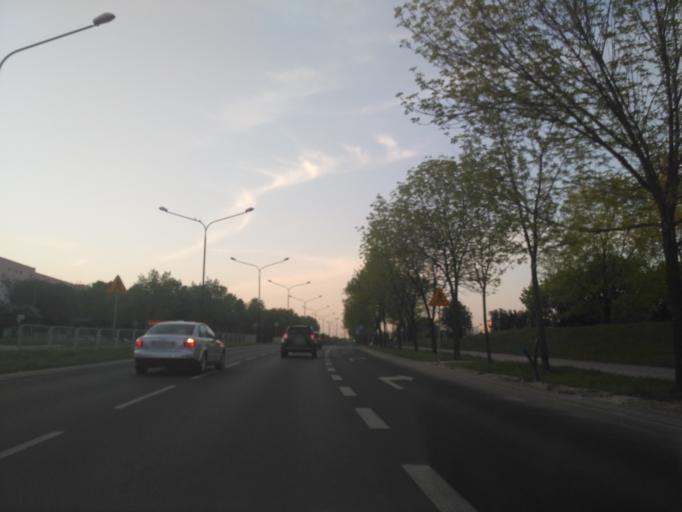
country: PL
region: Lublin Voivodeship
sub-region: Powiat lubelski
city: Lublin
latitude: 51.2644
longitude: 22.5585
